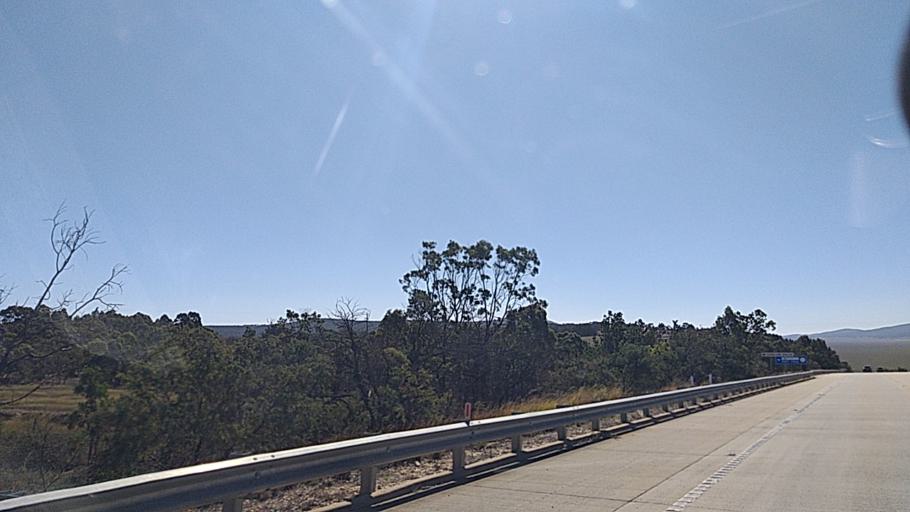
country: AU
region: New South Wales
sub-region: Yass Valley
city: Gundaroo
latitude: -35.1038
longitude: 149.3728
